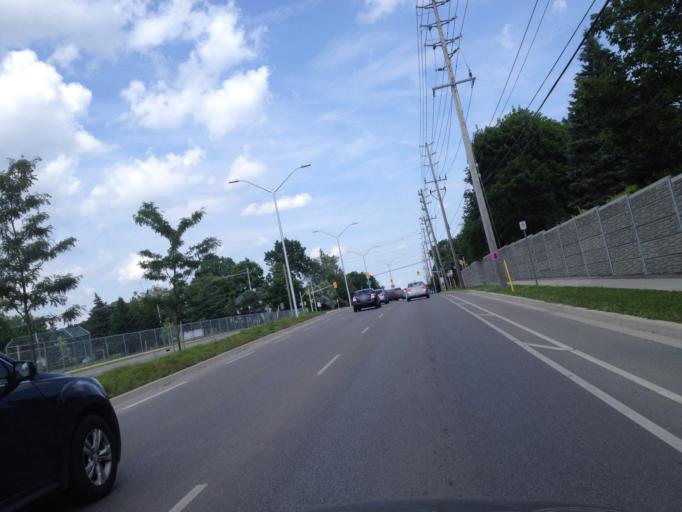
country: CA
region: Ontario
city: London
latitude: 42.9982
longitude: -81.2893
